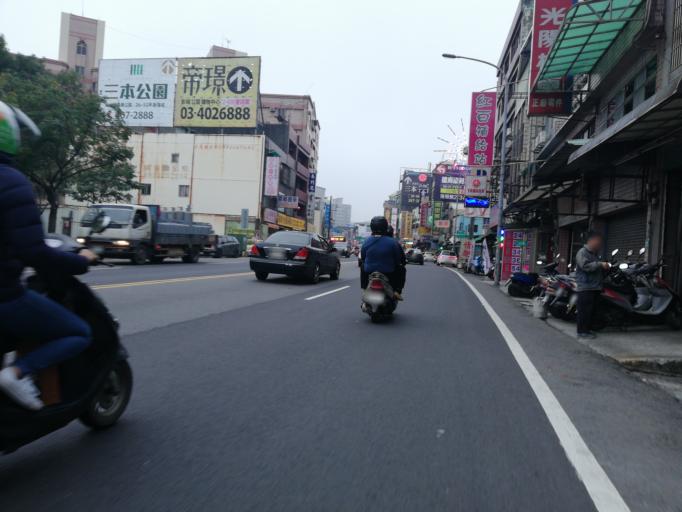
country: TW
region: Taiwan
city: Taoyuan City
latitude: 24.9798
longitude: 121.3049
